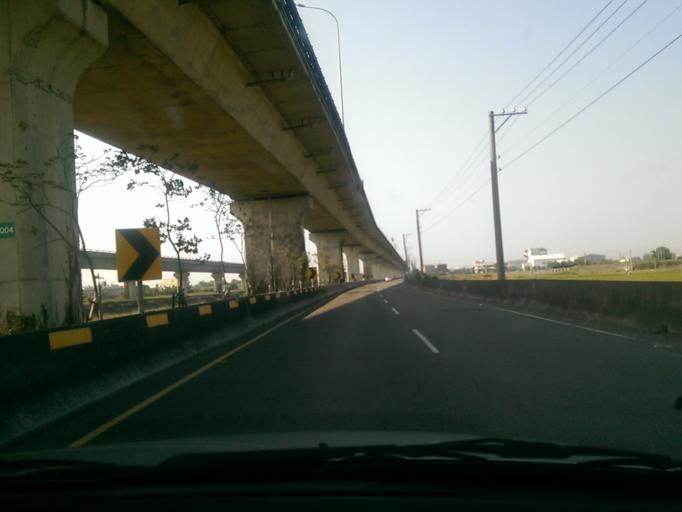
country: TW
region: Taiwan
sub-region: Changhua
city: Chang-hua
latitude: 23.9892
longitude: 120.5045
